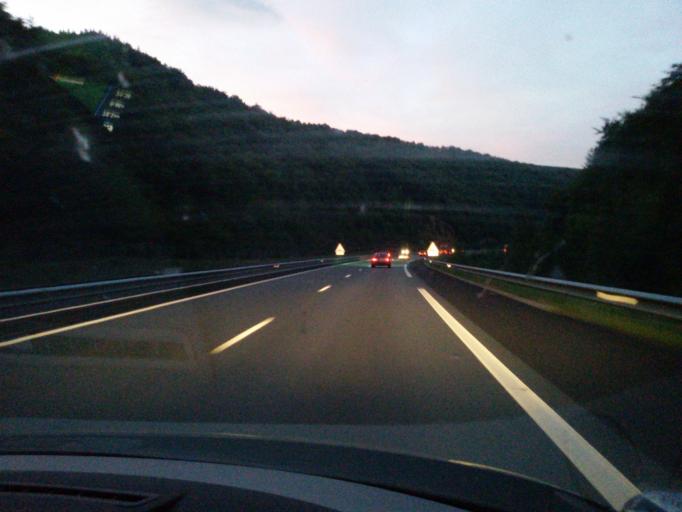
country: FR
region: Auvergne
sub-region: Departement du Cantal
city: Massiac
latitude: 45.1900
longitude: 3.1837
